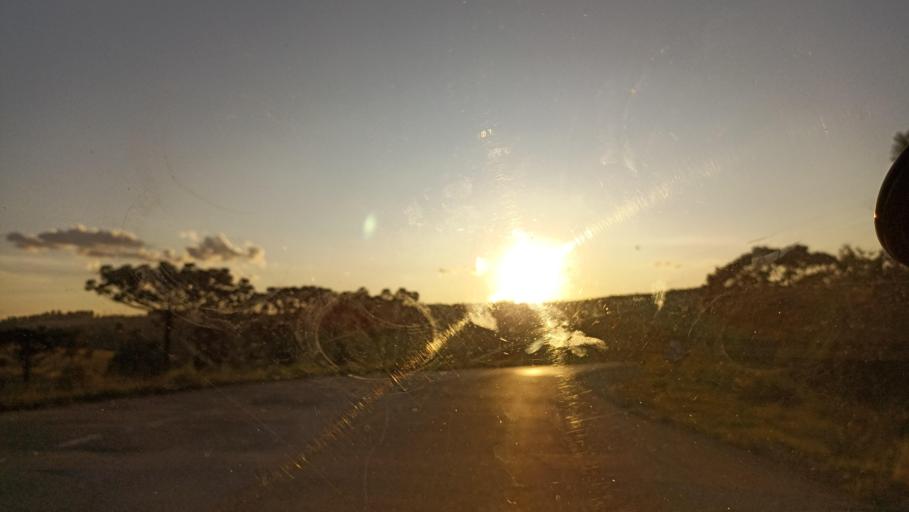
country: BR
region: Minas Gerais
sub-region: Sao Joao Del Rei
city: Sao Joao del Rei
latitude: -21.2303
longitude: -44.3779
